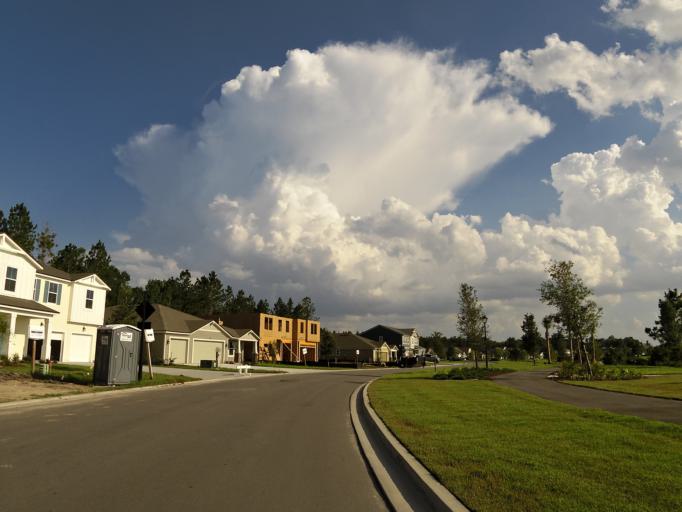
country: US
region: Florida
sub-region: Clay County
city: Green Cove Springs
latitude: 30.0293
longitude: -81.6299
